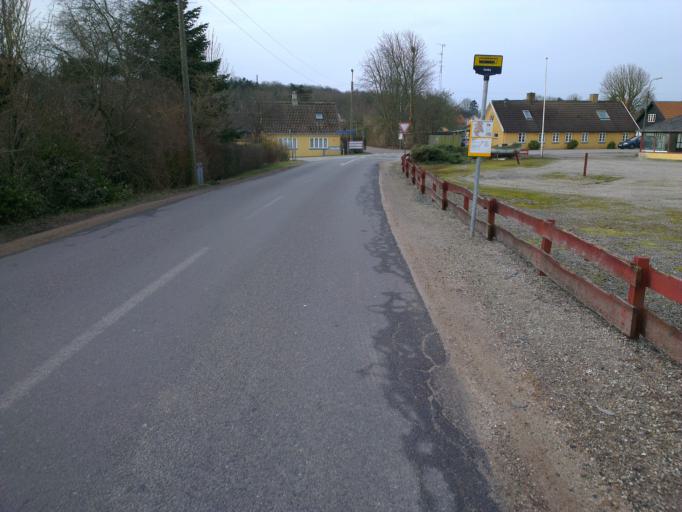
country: DK
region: Capital Region
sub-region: Frederikssund Kommune
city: Skibby
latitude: 55.7950
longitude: 11.9564
